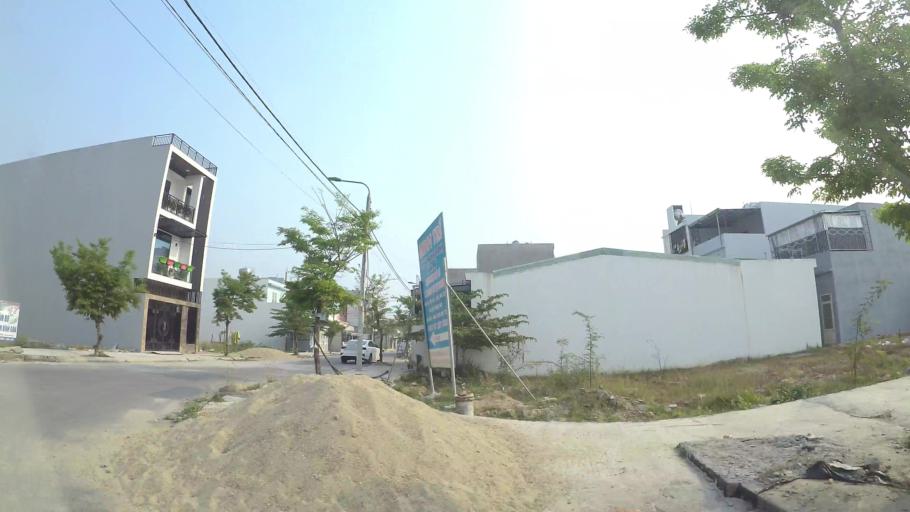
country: VN
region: Da Nang
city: Cam Le
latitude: 16.0073
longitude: 108.2261
